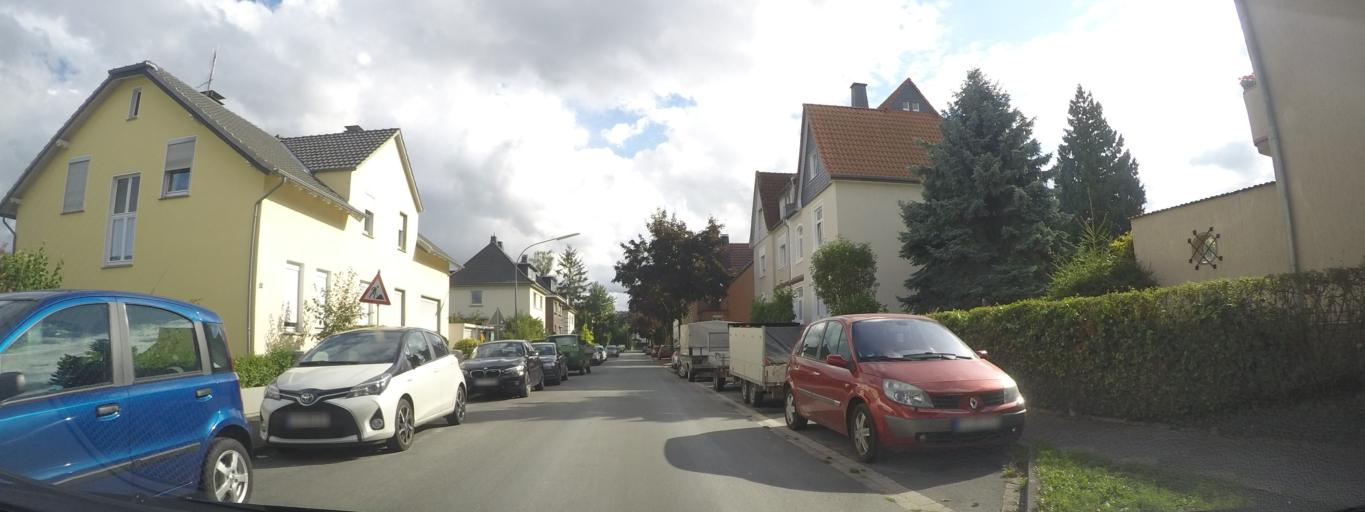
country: DE
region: North Rhine-Westphalia
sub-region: Regierungsbezirk Arnsberg
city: Lippstadt
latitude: 51.6825
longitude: 8.3415
